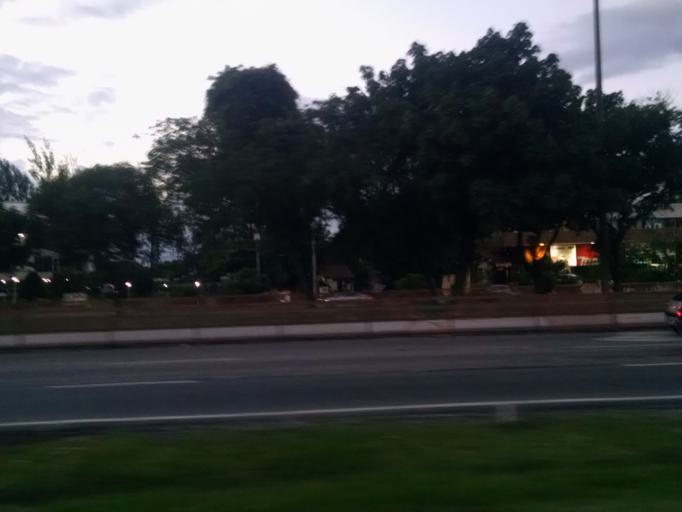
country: BR
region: Rio de Janeiro
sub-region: Rio De Janeiro
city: Rio de Janeiro
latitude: -23.0005
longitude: -43.3418
